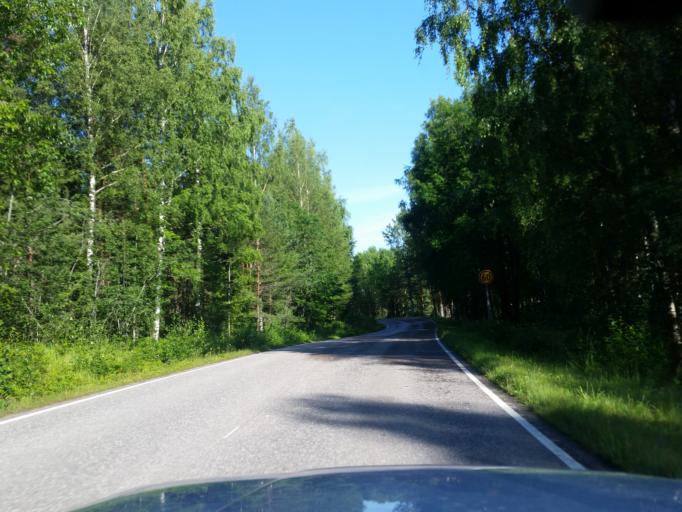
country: FI
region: Southern Savonia
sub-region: Savonlinna
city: Sulkava
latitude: 61.7932
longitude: 28.3822
